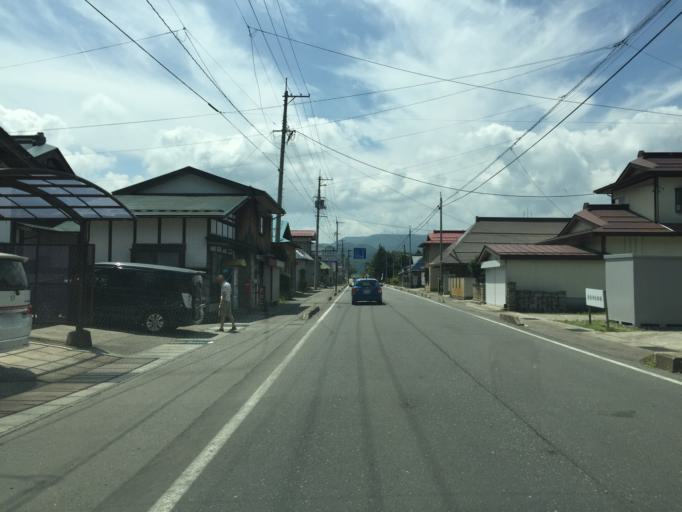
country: JP
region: Fukushima
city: Inawashiro
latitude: 37.3921
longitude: 140.0889
